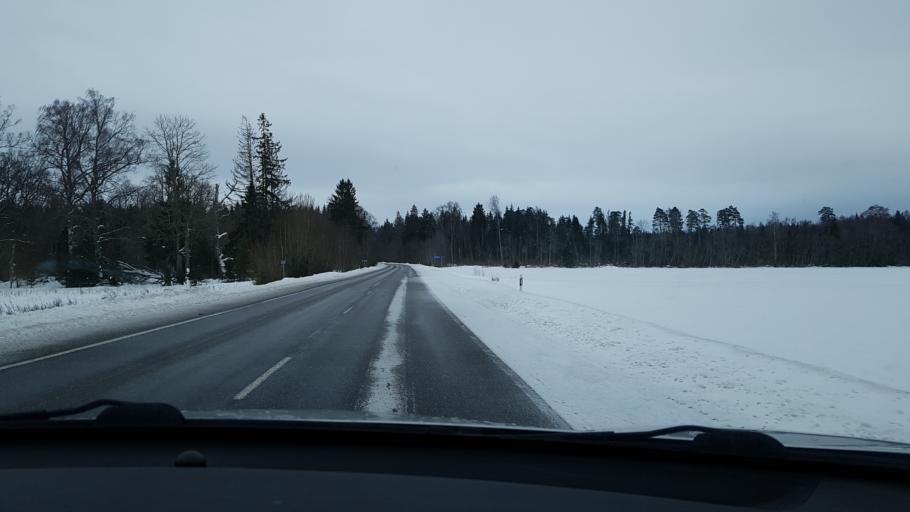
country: EE
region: Jaervamaa
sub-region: Jaerva-Jaani vald
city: Jarva-Jaani
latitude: 59.1000
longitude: 25.8169
